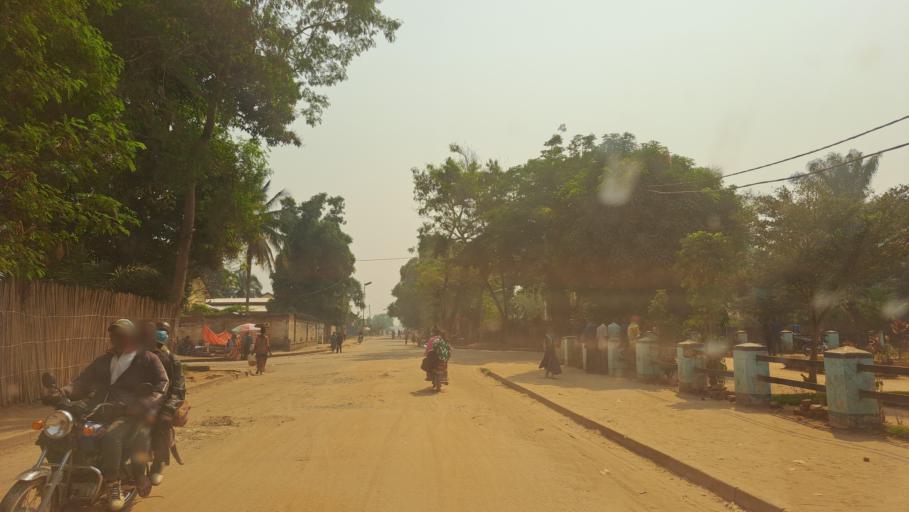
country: CD
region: Kasai-Occidental
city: Kananga
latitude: -5.9012
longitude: 22.4062
